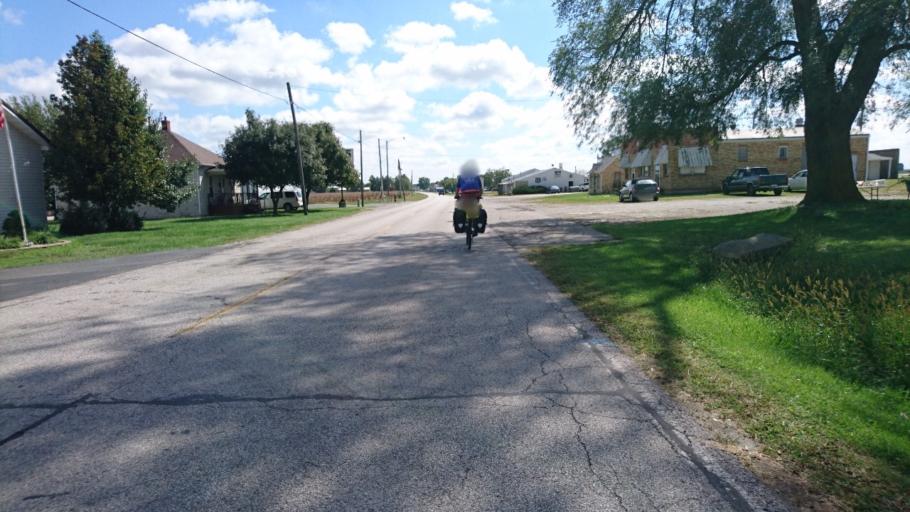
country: US
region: Illinois
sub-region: Montgomery County
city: Litchfield
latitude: 39.1696
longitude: -89.6669
